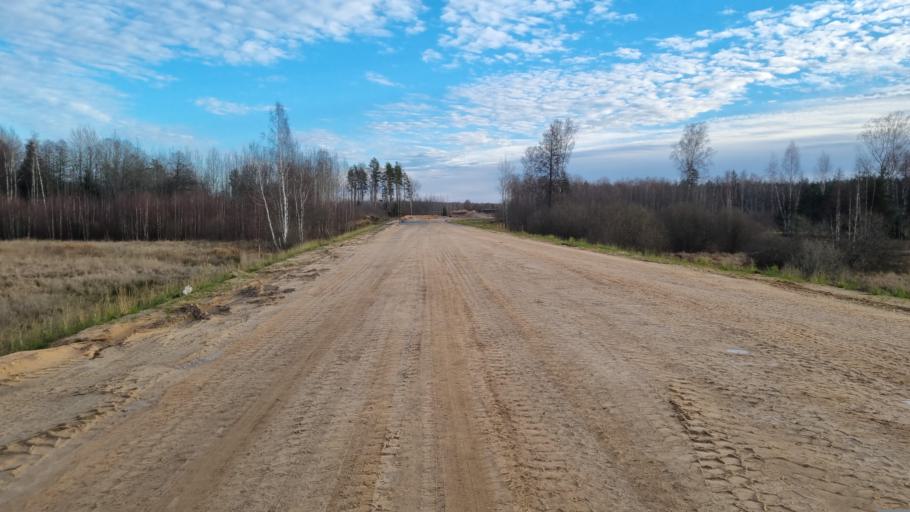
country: LV
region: Kekava
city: Kekava
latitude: 56.7833
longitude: 24.2316
